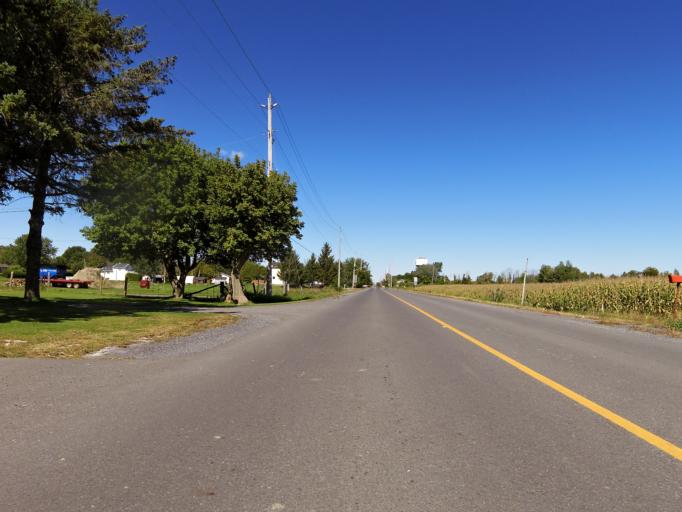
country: CA
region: Ontario
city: Casselman
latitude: 45.2651
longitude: -75.2703
